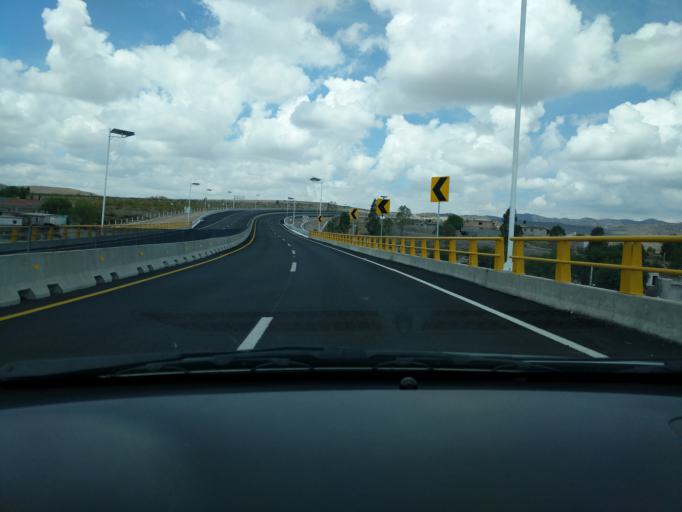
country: MX
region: San Luis Potosi
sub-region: Mexquitic de Carmona
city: Guadalupe Victoria
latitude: 22.1634
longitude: -101.0602
